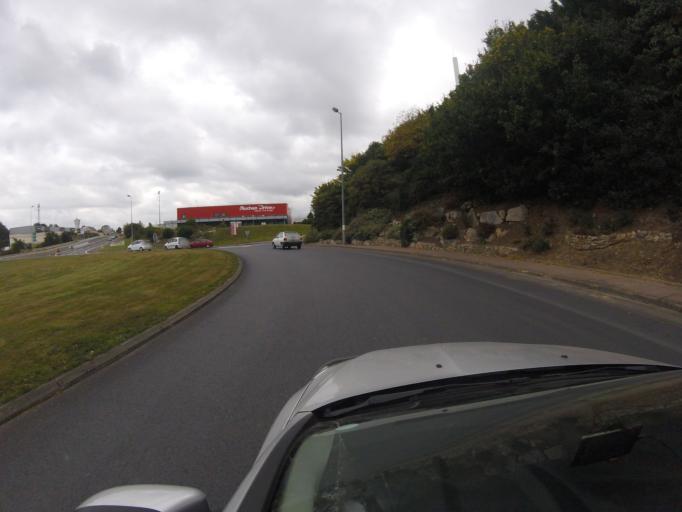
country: FR
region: Lower Normandy
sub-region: Departement de la Manche
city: La Glacerie
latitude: 49.6052
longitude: -1.5990
